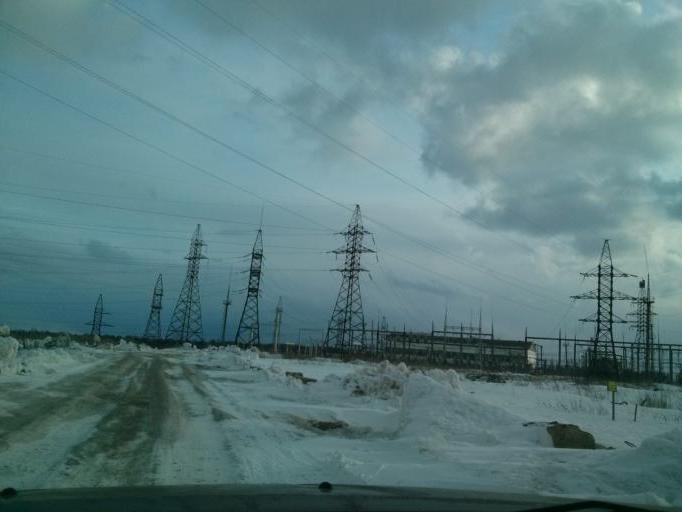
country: RU
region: Nizjnij Novgorod
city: Afonino
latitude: 56.2662
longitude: 44.0308
